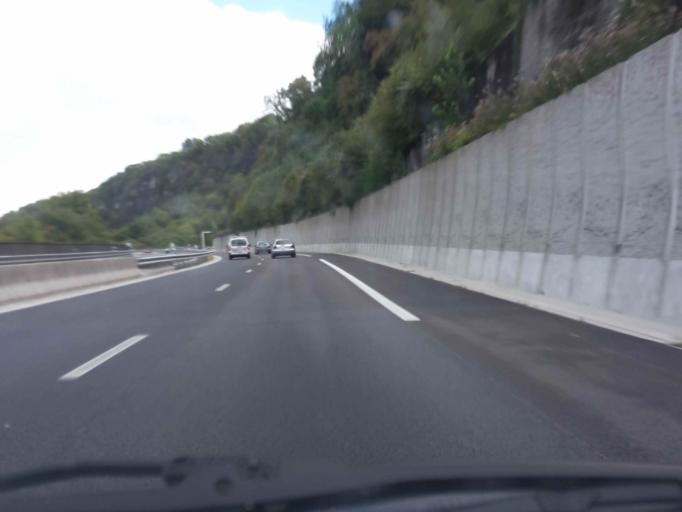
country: FR
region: Franche-Comte
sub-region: Departement du Doubs
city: Beure
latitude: 47.2159
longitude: 6.0153
